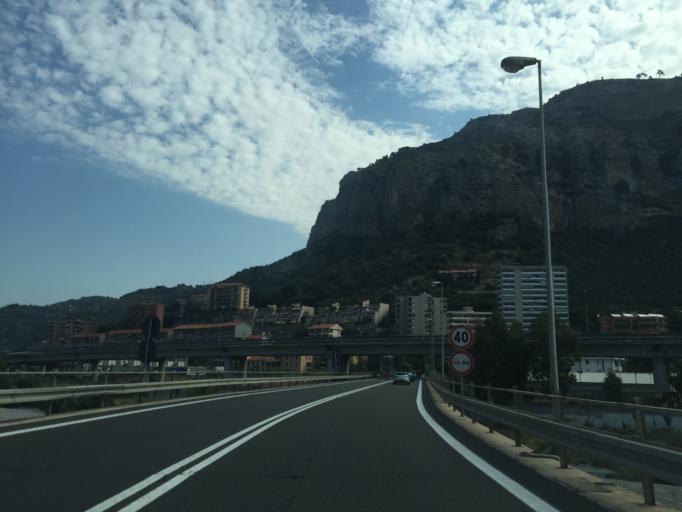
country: IT
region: Liguria
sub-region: Provincia di Imperia
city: Ventimiglia
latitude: 43.8053
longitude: 7.5927
